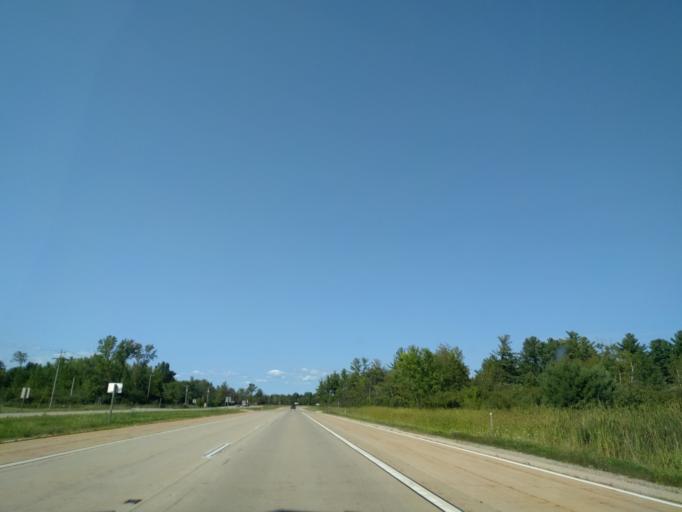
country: US
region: Wisconsin
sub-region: Oconto County
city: Oconto
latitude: 44.8620
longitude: -87.8991
